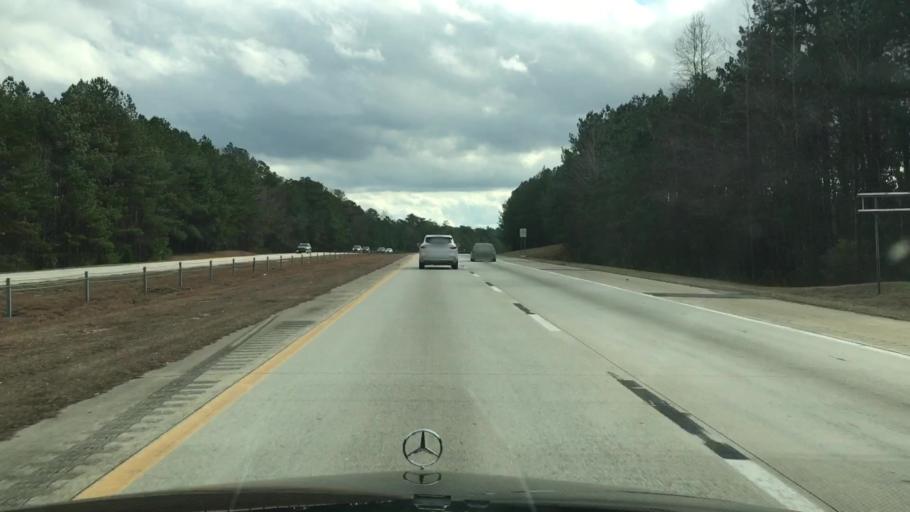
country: US
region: North Carolina
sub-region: Wake County
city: Garner
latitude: 35.6809
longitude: -78.5667
